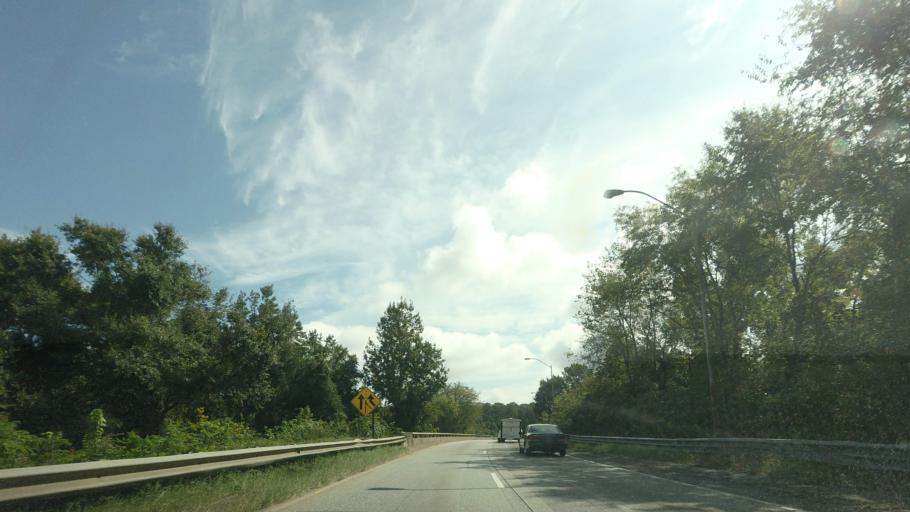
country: US
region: Georgia
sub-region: Bibb County
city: Macon
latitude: 32.8545
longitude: -83.6378
